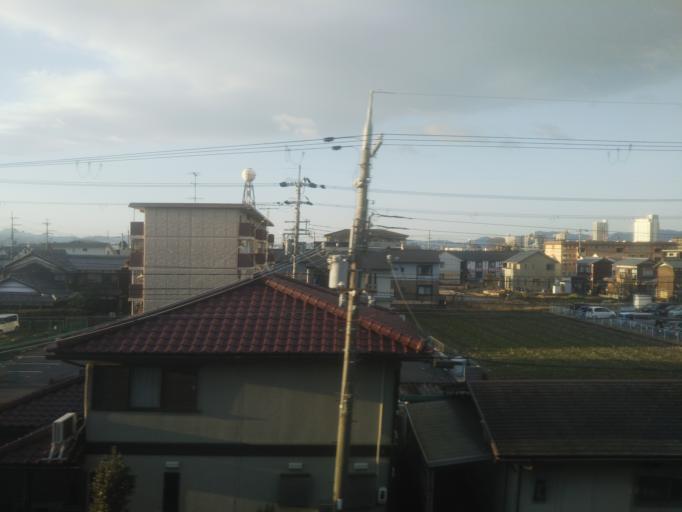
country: JP
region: Shiga Prefecture
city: Kusatsu
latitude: 35.0291
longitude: 135.9794
